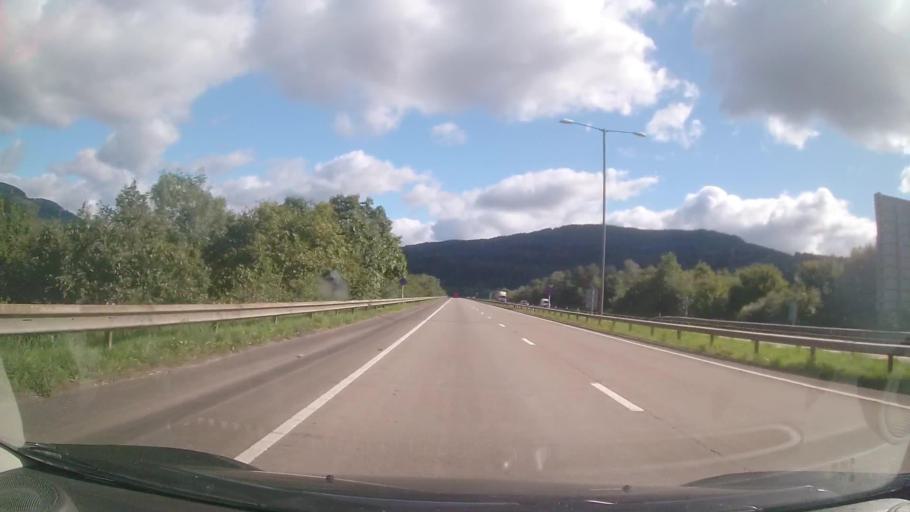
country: GB
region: Wales
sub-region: Neath Port Talbot
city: Resolven
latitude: 51.7146
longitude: -3.6945
